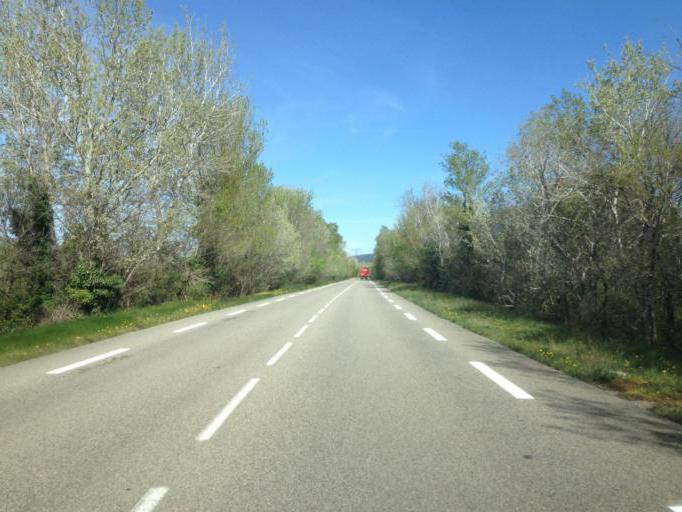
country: FR
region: Provence-Alpes-Cote d'Azur
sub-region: Departement du Vaucluse
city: Caderousse
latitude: 44.1162
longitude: 4.7219
